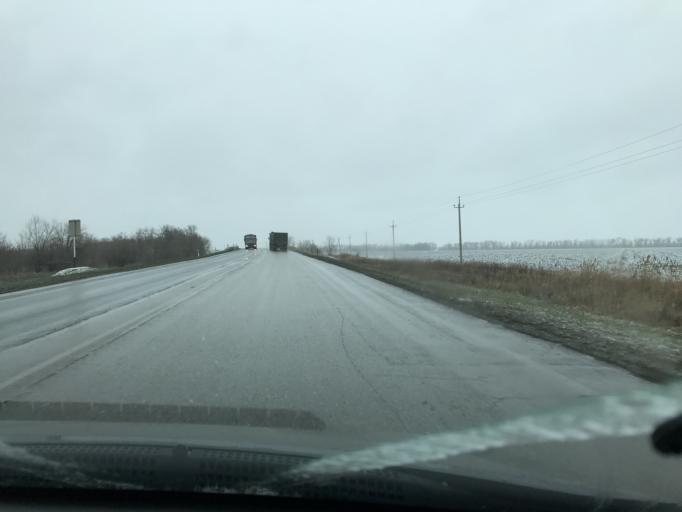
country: RU
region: Rostov
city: Mechetinskaya
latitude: 46.7669
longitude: 40.4261
